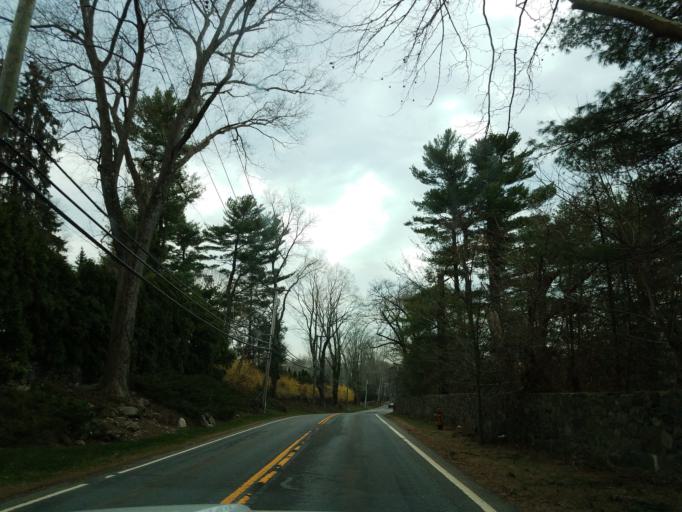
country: US
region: Connecticut
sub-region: Fairfield County
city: Glenville
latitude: 41.0597
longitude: -73.6392
